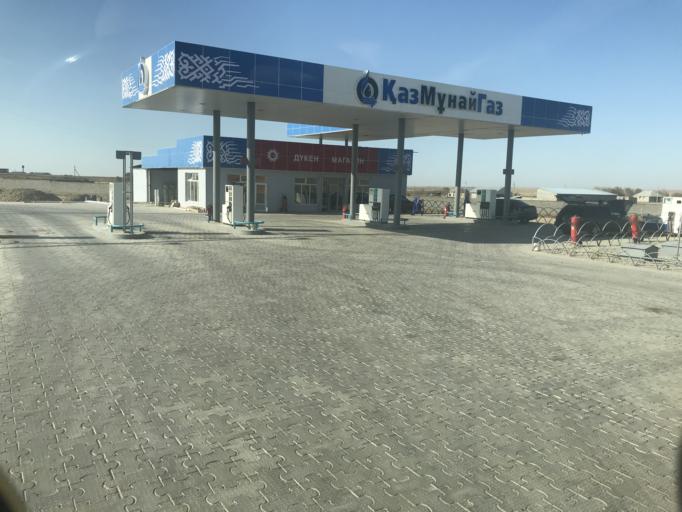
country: KZ
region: Ongtustik Qazaqstan
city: Shymkent
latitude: 42.4574
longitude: 69.6010
